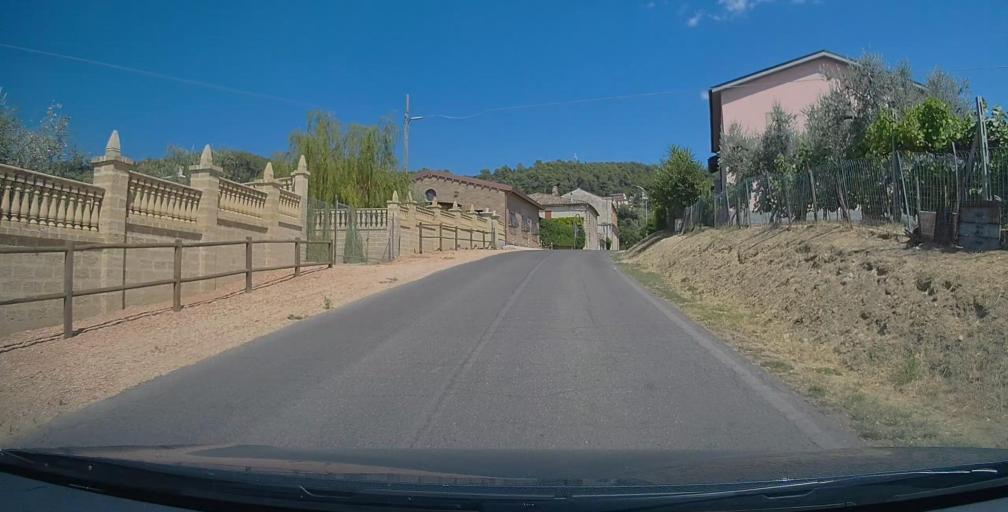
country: IT
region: Umbria
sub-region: Provincia di Terni
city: Calvi dell'Umbria
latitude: 42.4077
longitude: 12.5612
